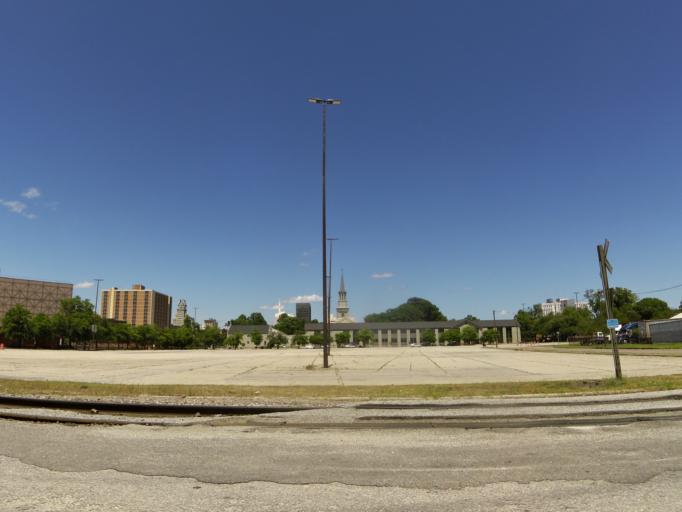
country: US
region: Georgia
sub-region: Richmond County
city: Augusta
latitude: 33.4684
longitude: -81.9658
